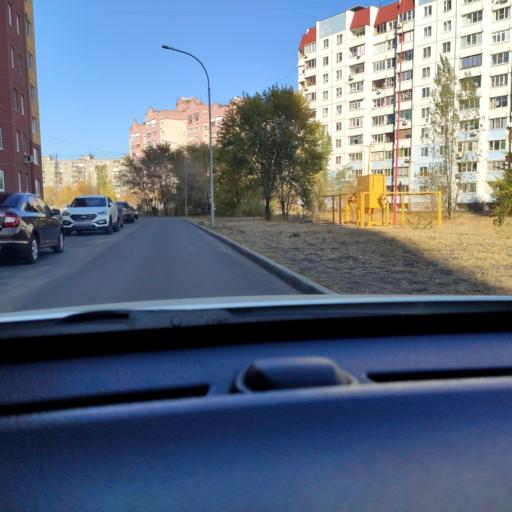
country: RU
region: Voronezj
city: Voronezh
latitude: 51.7164
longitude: 39.2673
